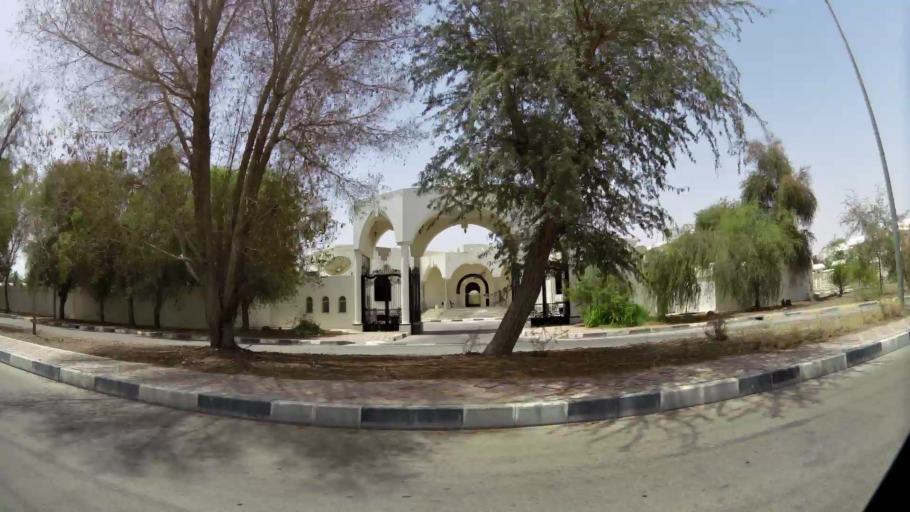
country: AE
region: Abu Dhabi
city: Al Ain
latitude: 24.1997
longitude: 55.7383
